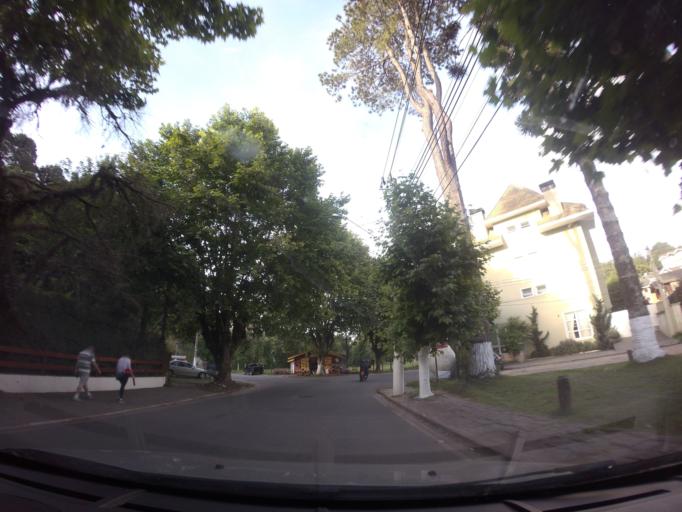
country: BR
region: Sao Paulo
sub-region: Campos Do Jordao
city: Campos do Jordao
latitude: -22.7244
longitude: -45.5679
